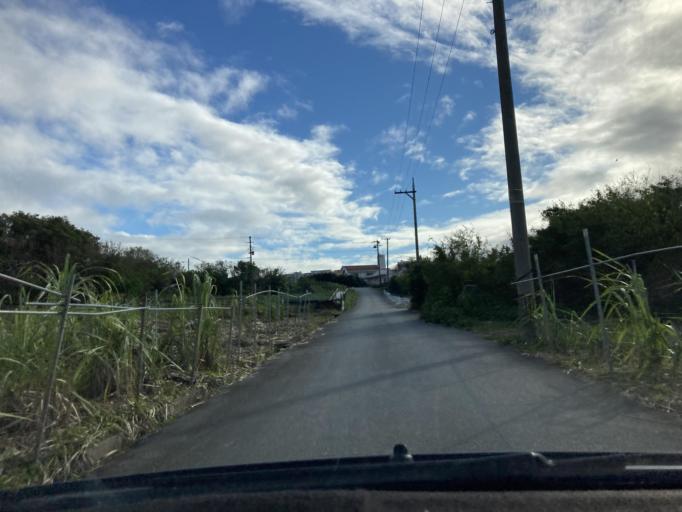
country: JP
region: Okinawa
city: Itoman
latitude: 26.1071
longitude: 127.6623
